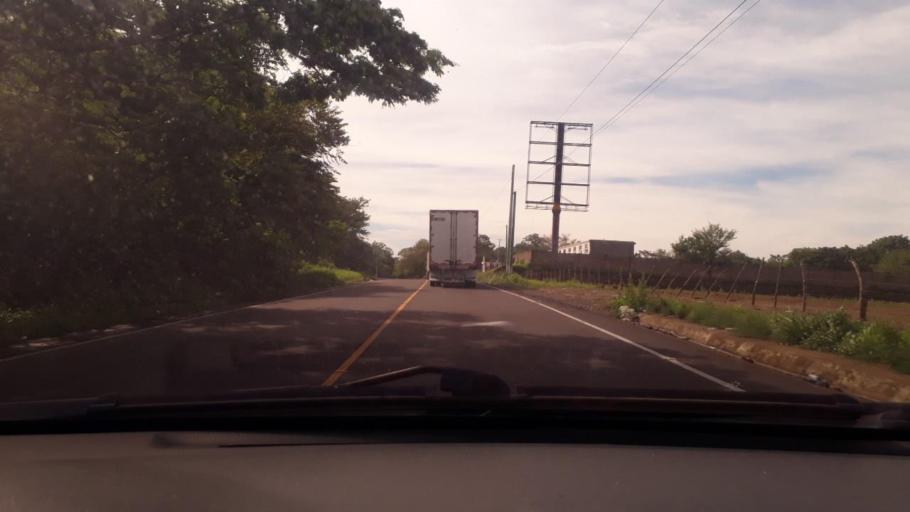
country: SV
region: Ahuachapan
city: San Francisco Menendez
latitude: 13.8803
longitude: -90.1308
